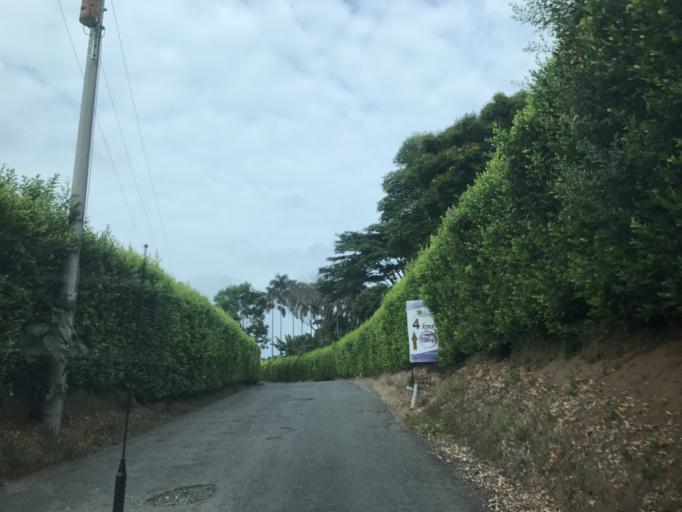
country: CO
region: Quindio
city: Montenegro
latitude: 4.5483
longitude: -75.8038
